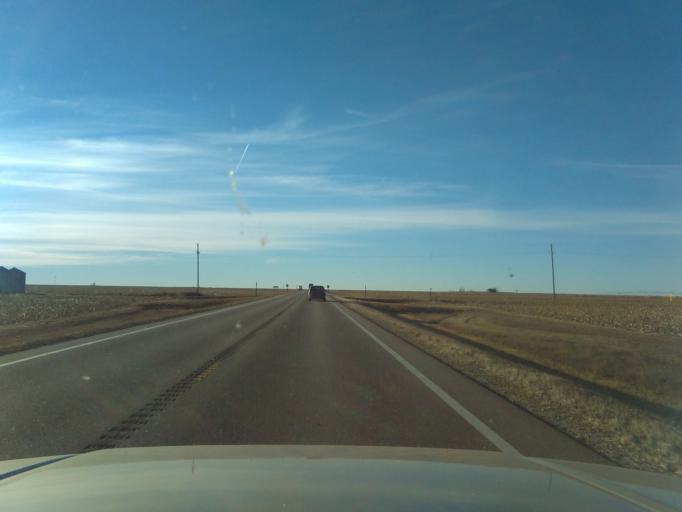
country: US
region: Kansas
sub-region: Thomas County
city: Colby
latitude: 39.4649
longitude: -100.7566
